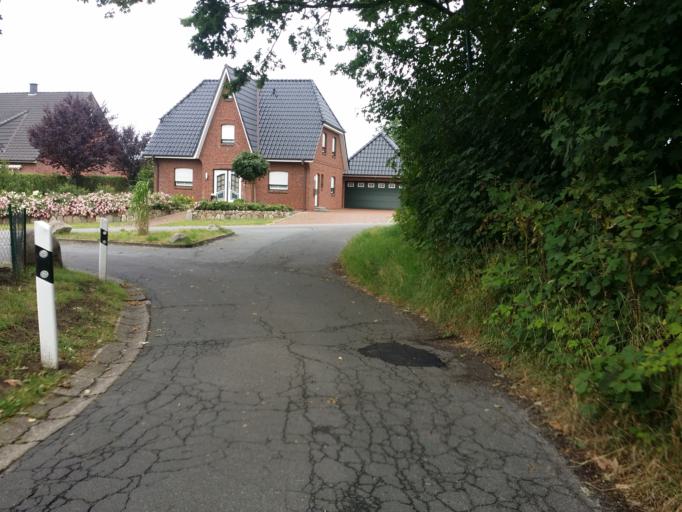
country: DE
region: Schleswig-Holstein
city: Oldendorf
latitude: 53.9565
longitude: 9.4548
